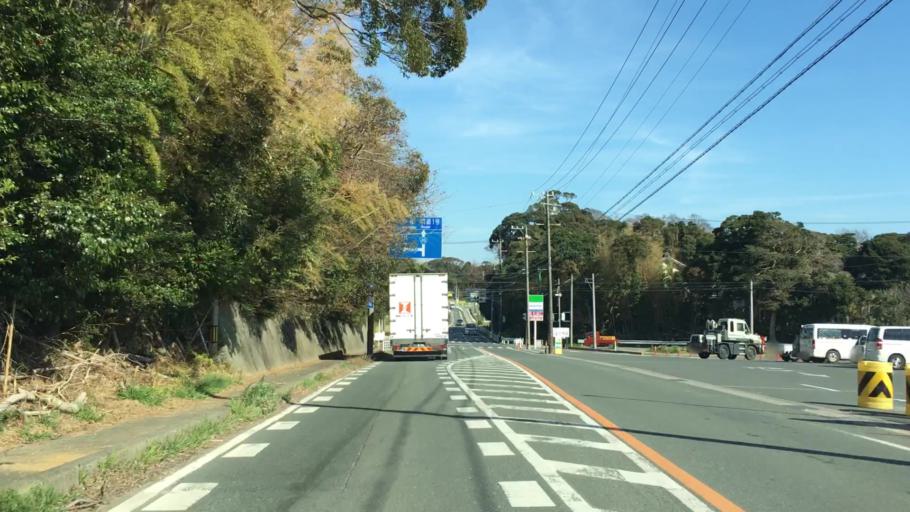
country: JP
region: Shizuoka
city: Kosai-shi
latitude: 34.6840
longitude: 137.4625
